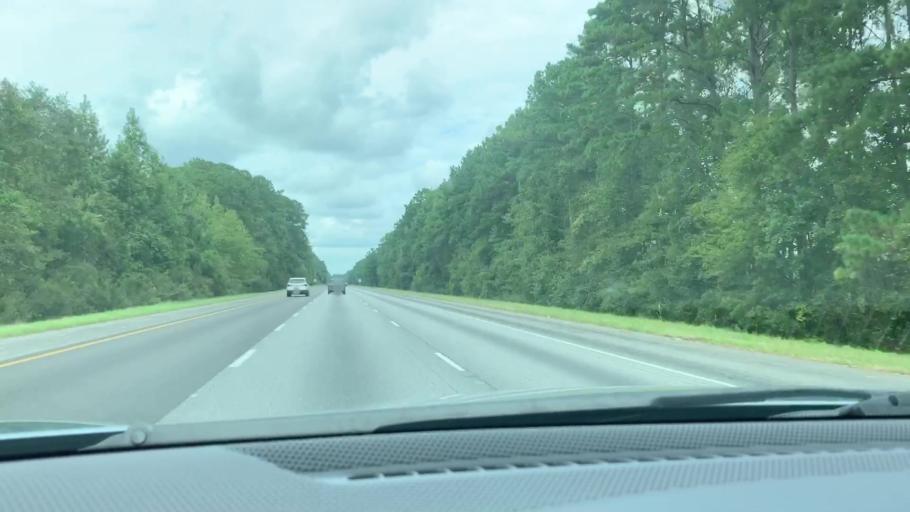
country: US
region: Georgia
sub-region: Bryan County
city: Richmond Hill
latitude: 31.8788
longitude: -81.3300
